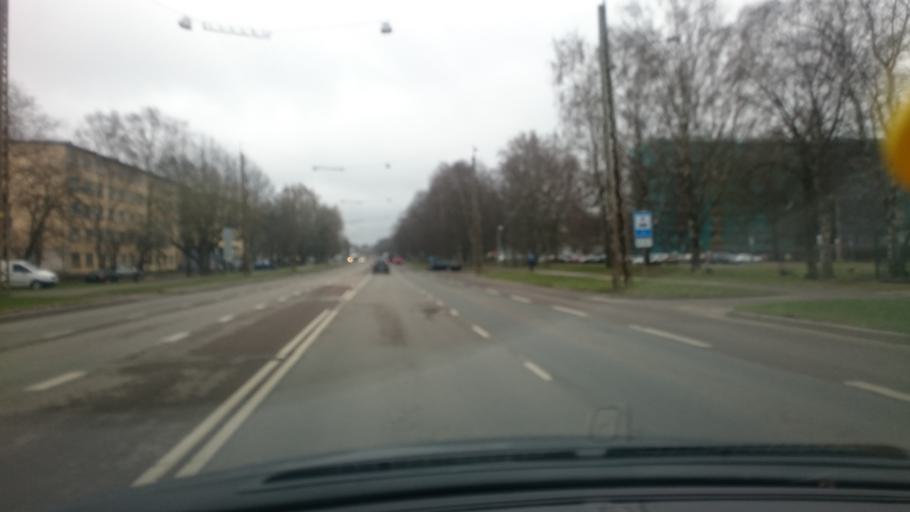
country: EE
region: Harju
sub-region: Tallinna linn
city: Tallinn
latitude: 59.4378
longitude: 24.7097
